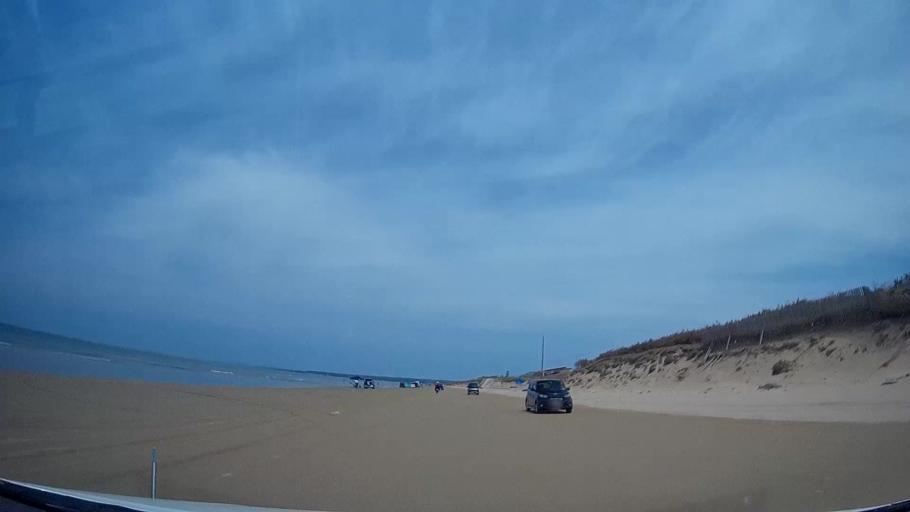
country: JP
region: Ishikawa
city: Hakui
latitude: 36.8609
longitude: 136.7569
